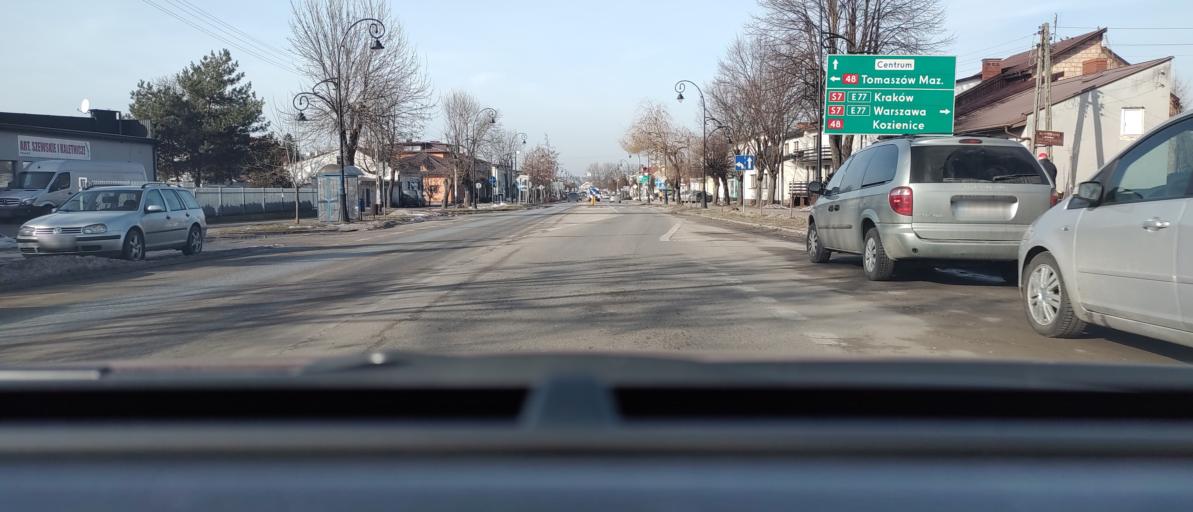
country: PL
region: Masovian Voivodeship
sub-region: Powiat bialobrzeski
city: Bialobrzegi
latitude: 51.6452
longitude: 20.9575
